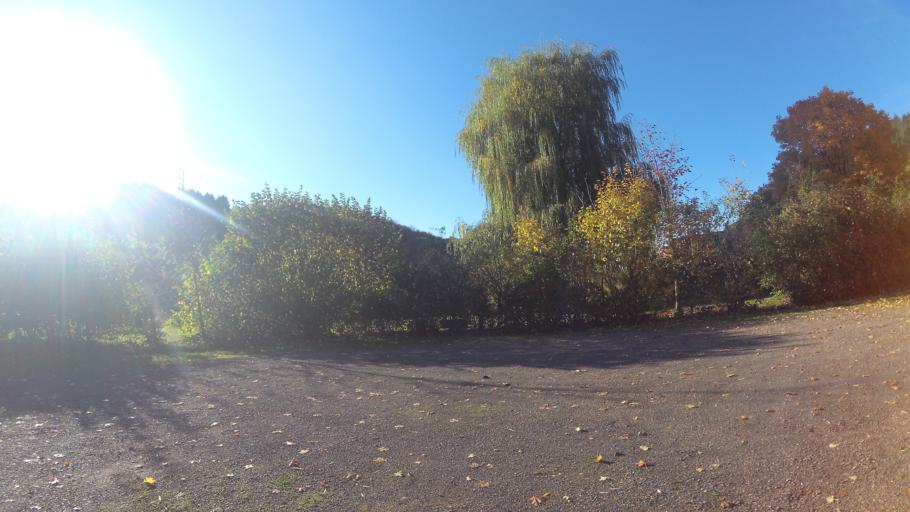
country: DE
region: Saarland
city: Losheim
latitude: 49.4734
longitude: 6.7202
